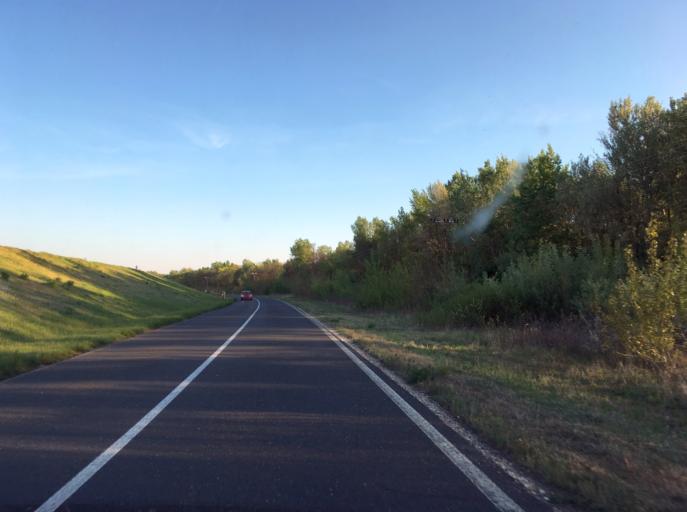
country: HU
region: Gyor-Moson-Sopron
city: Rajka
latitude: 48.0073
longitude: 17.2523
